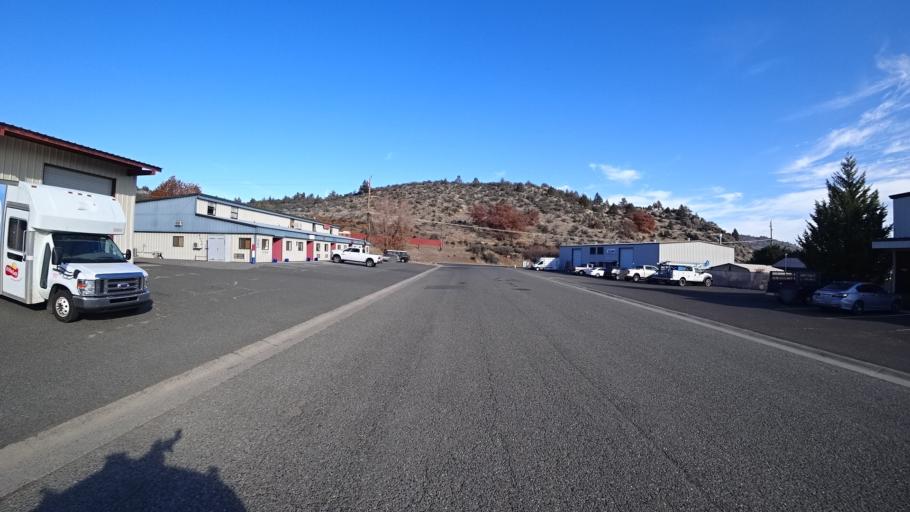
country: US
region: California
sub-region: Siskiyou County
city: Yreka
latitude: 41.7110
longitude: -122.6467
